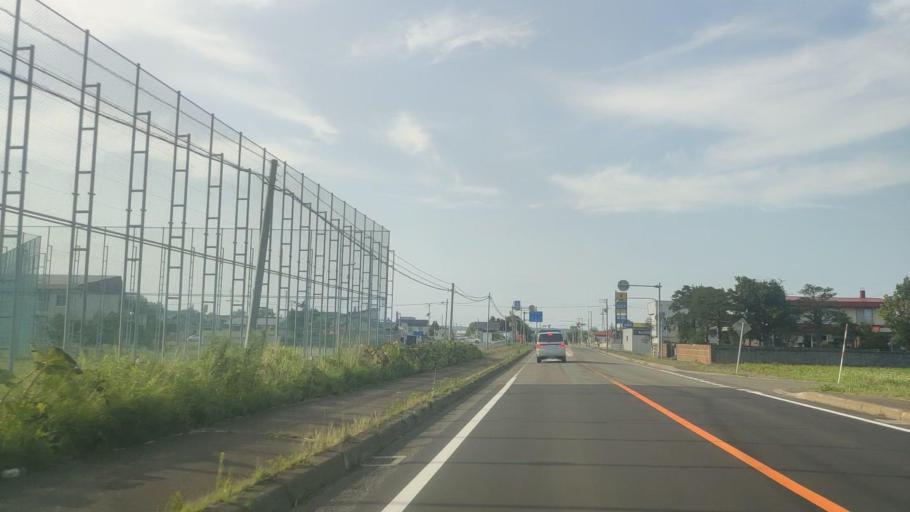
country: JP
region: Hokkaido
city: Iwamizawa
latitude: 43.0066
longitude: 141.7898
